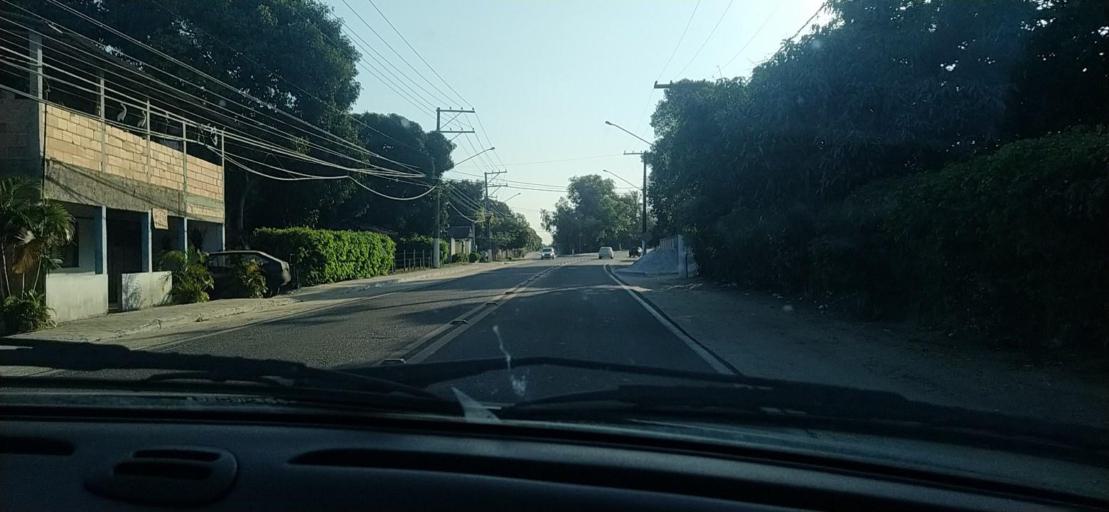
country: BR
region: Espirito Santo
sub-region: Conceicao Da Barra
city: Conceicao da Barra
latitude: -18.5679
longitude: -39.7487
